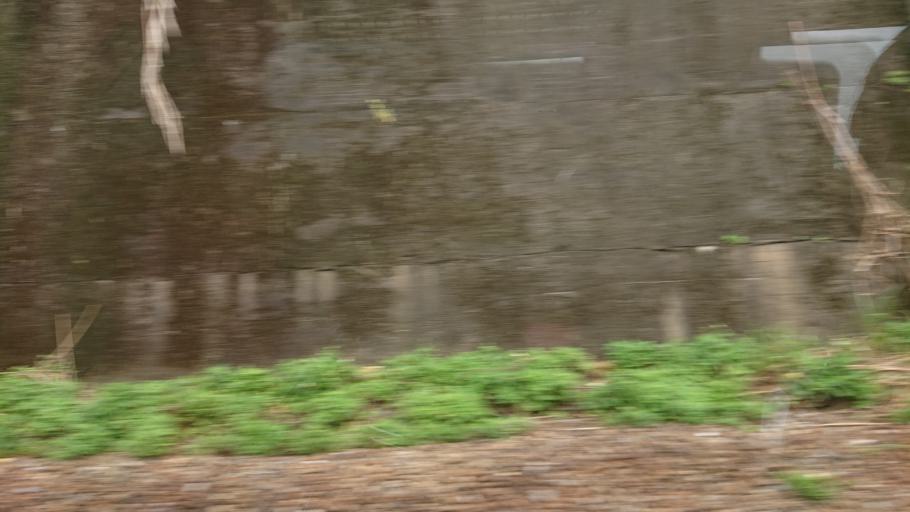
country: TW
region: Taiwan
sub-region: Yilan
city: Yilan
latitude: 24.9157
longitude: 121.8804
